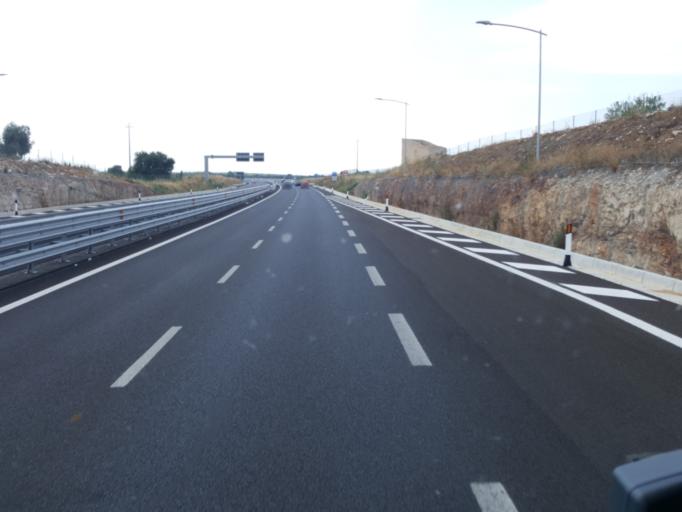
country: IT
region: Apulia
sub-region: Provincia di Bari
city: Palo del Colle
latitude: 41.0446
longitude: 16.7022
